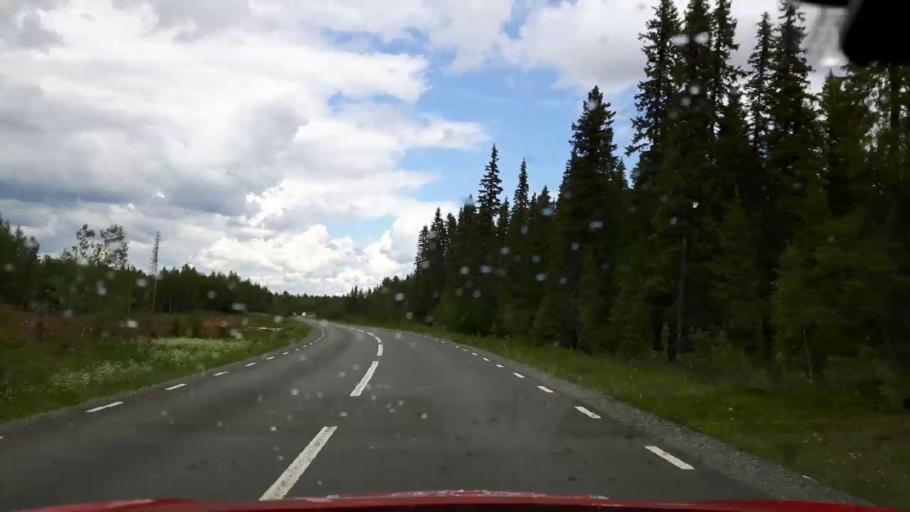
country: SE
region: Jaemtland
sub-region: Krokoms Kommun
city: Krokom
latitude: 63.5829
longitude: 14.2923
